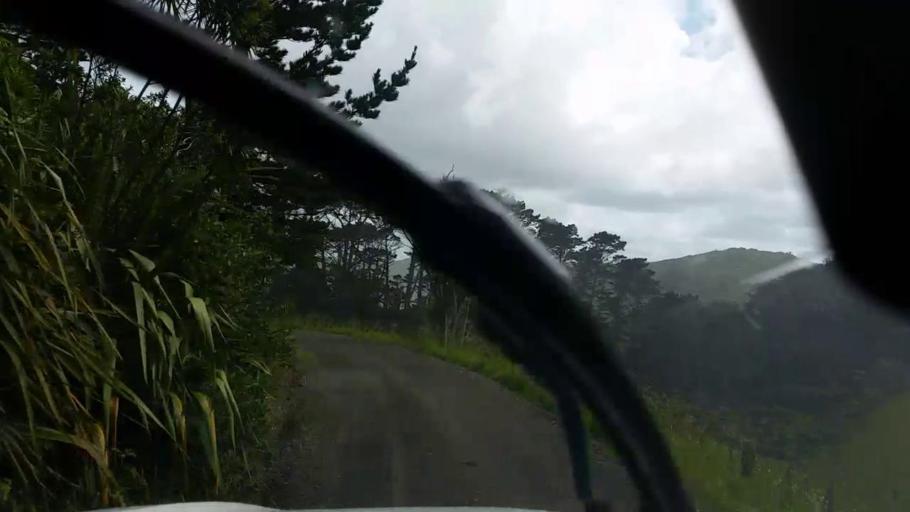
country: NZ
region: Auckland
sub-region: Auckland
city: Muriwai Beach
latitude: -36.9256
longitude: 174.4589
